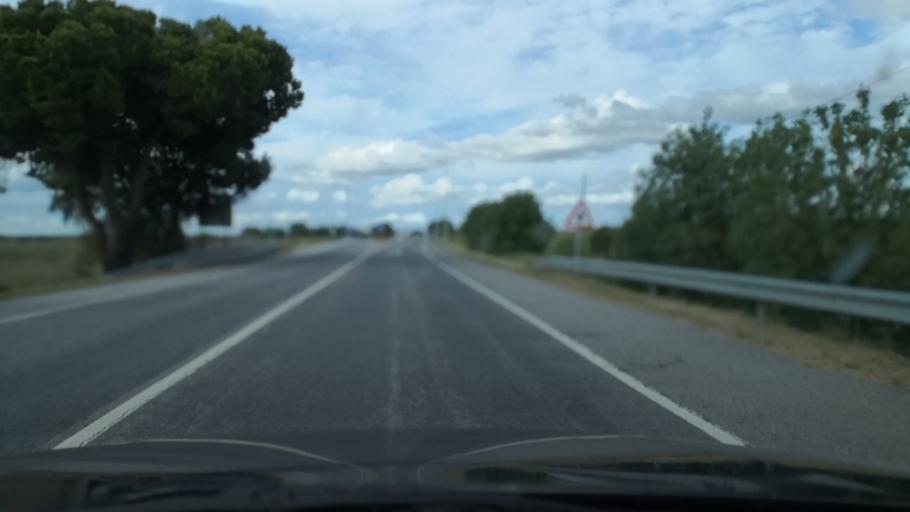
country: PT
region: Evora
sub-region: Evora
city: Evora
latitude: 38.6398
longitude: -7.8530
